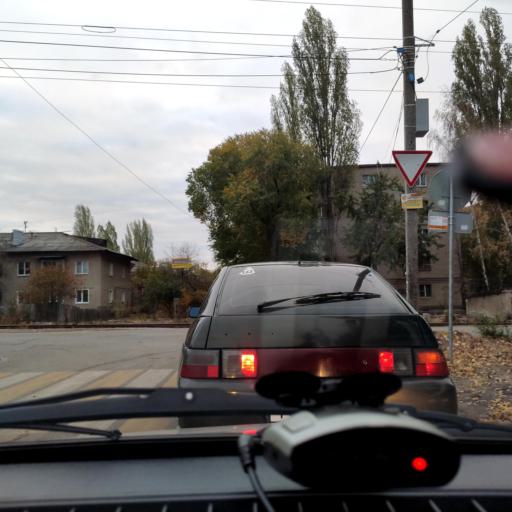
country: RU
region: Voronezj
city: Voronezh
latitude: 51.6402
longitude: 39.1548
